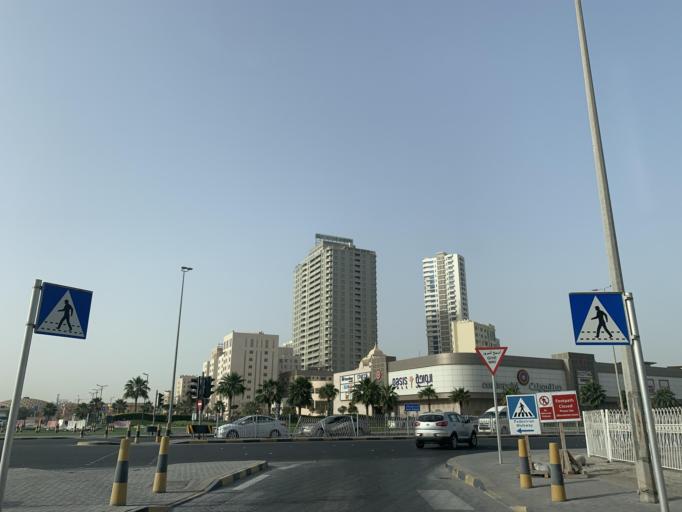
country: BH
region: Manama
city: Manama
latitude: 26.2170
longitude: 50.6009
